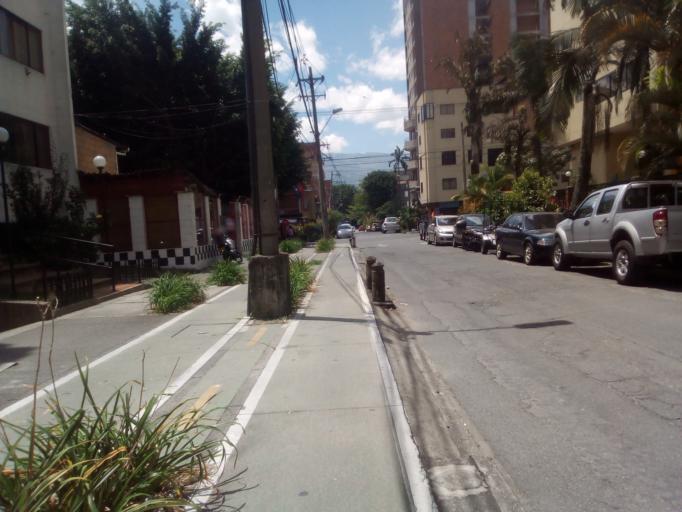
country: CO
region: Antioquia
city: Medellin
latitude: 6.2511
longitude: -75.5926
